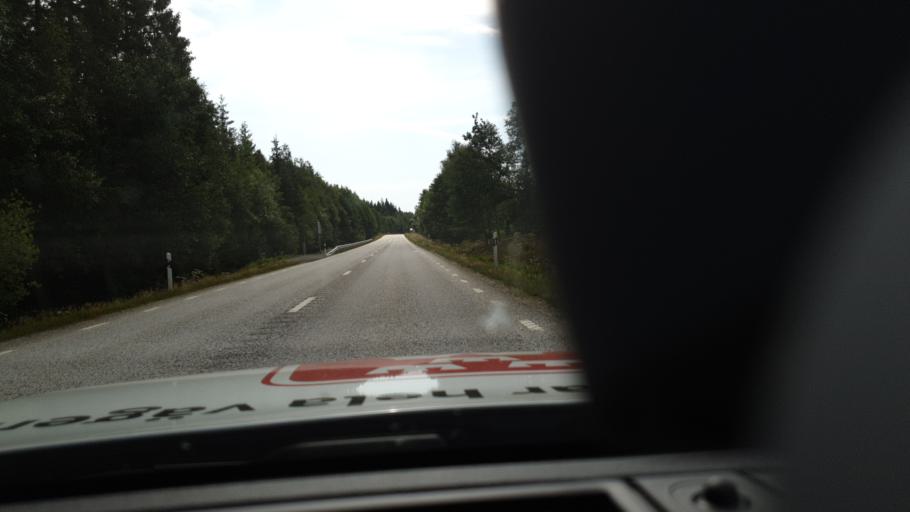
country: SE
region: Joenkoeping
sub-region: Nassjo Kommun
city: Nassjo
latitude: 57.6134
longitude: 14.8185
